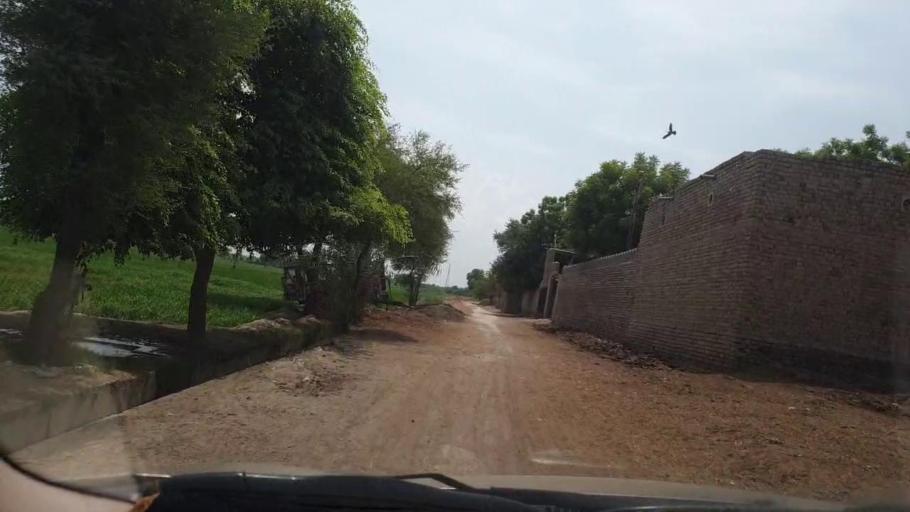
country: PK
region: Sindh
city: Larkana
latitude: 27.5904
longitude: 68.1205
